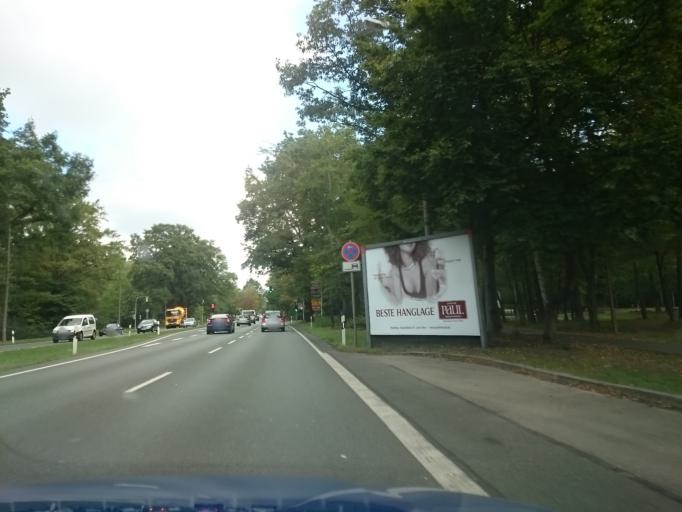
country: DE
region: Bavaria
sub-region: Regierungsbezirk Mittelfranken
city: Nuernberg
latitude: 49.4240
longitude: 11.1052
